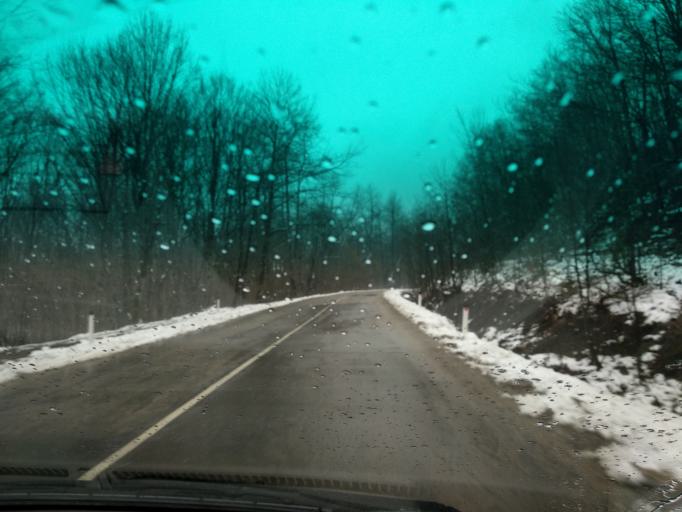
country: RU
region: Krasnodarskiy
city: Khadyzhensk
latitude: 44.2101
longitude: 39.4114
